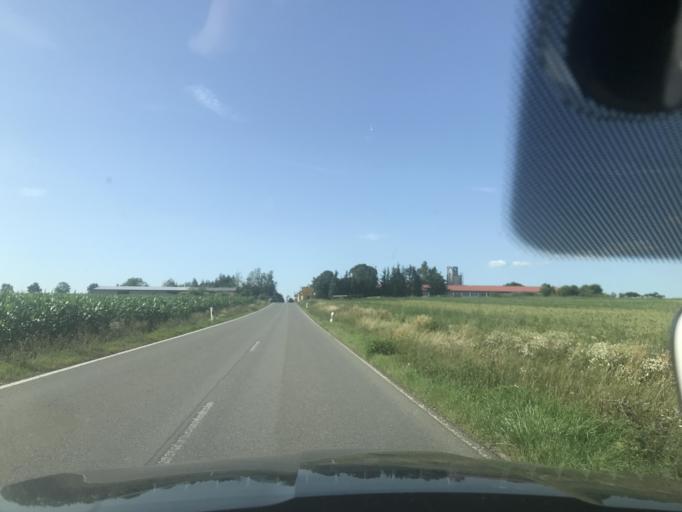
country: DE
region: Saxony-Anhalt
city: Gross Quenstedt
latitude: 51.9161
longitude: 11.1454
